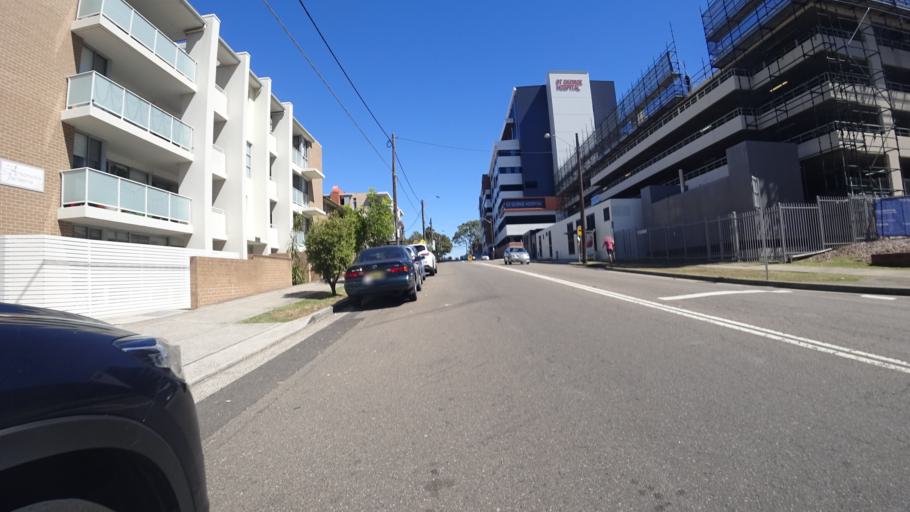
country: AU
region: New South Wales
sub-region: Kogarah
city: Beverly Park
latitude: -33.9685
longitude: 151.1336
